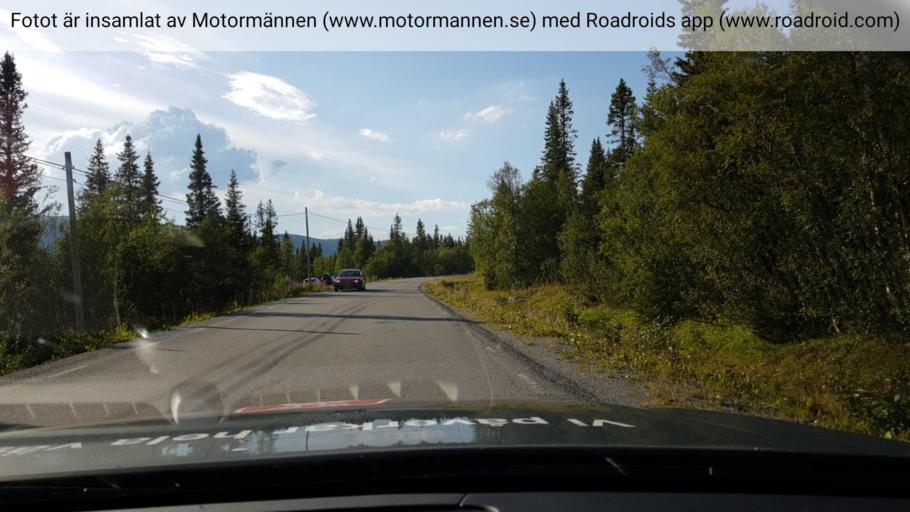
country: SE
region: Jaemtland
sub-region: Are Kommun
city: Are
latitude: 63.4175
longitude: 13.0226
